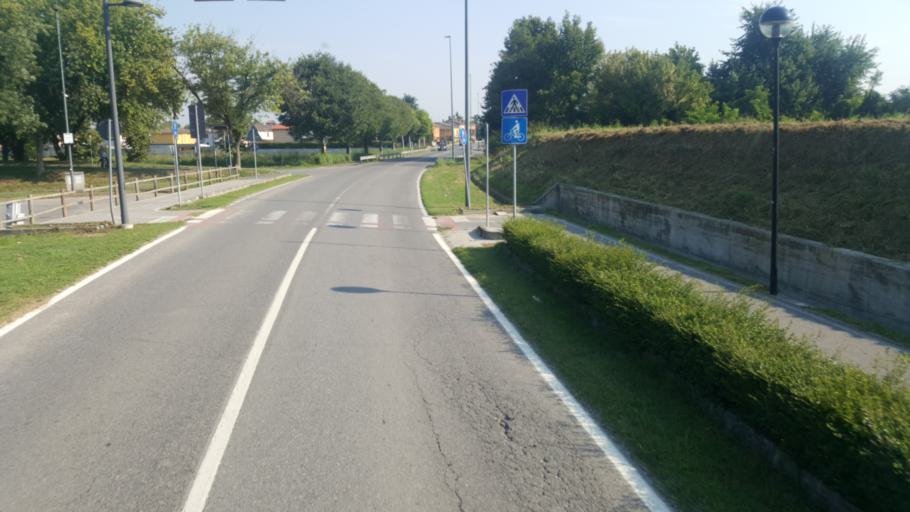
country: IT
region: Lombardy
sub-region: Provincia di Cremona
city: Robecco d'Oglio
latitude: 45.2544
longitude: 10.0727
